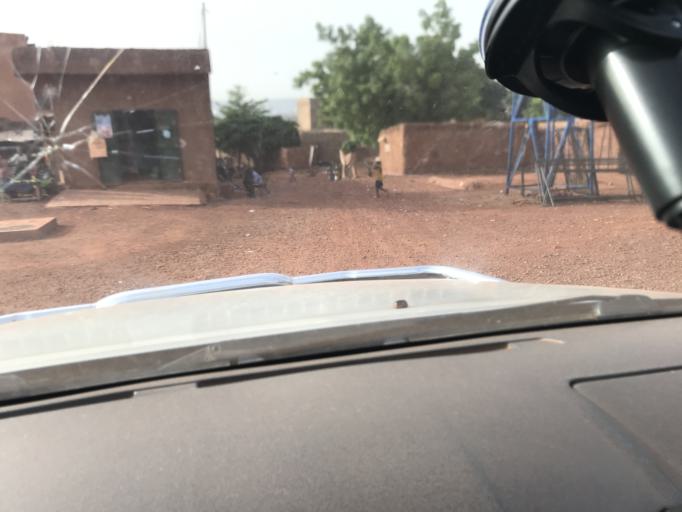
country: ML
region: Bamako
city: Bamako
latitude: 12.5896
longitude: -8.0078
